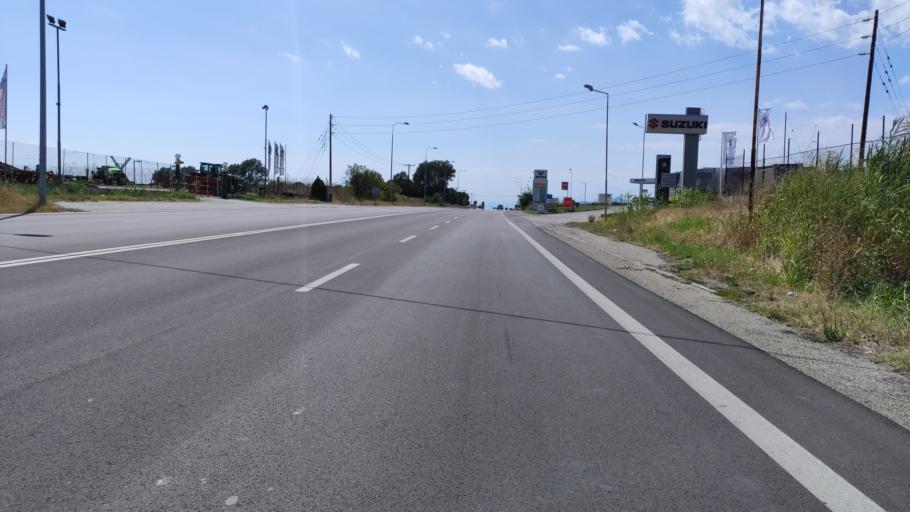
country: GR
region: East Macedonia and Thrace
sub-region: Nomos Rodopis
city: Komotini
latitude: 41.1085
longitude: 25.3557
